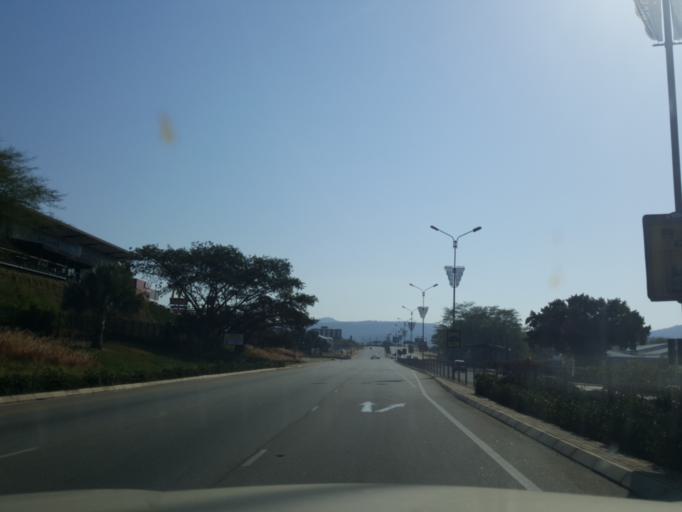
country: ZA
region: Mpumalanga
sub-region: Ehlanzeni District
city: Nelspruit
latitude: -25.4434
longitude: 30.9636
